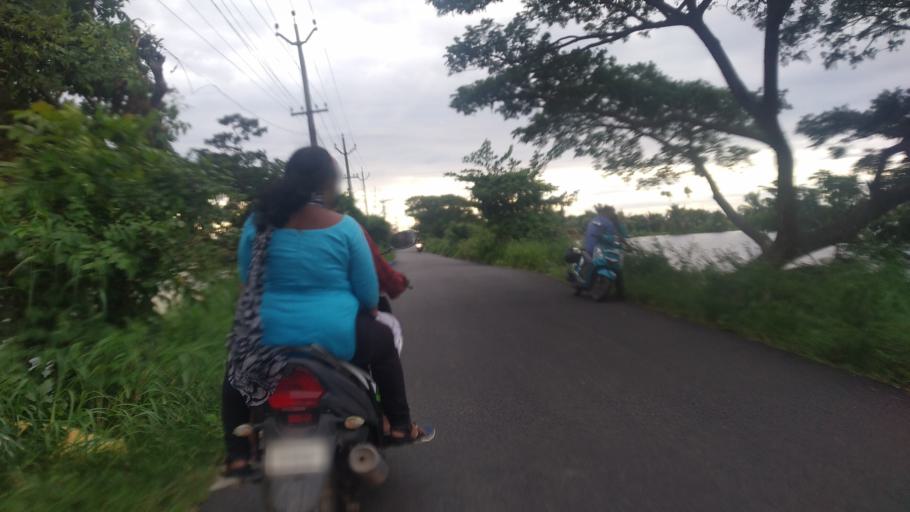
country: IN
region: Kerala
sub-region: Alappuzha
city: Arukutti
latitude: 9.8592
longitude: 76.2825
